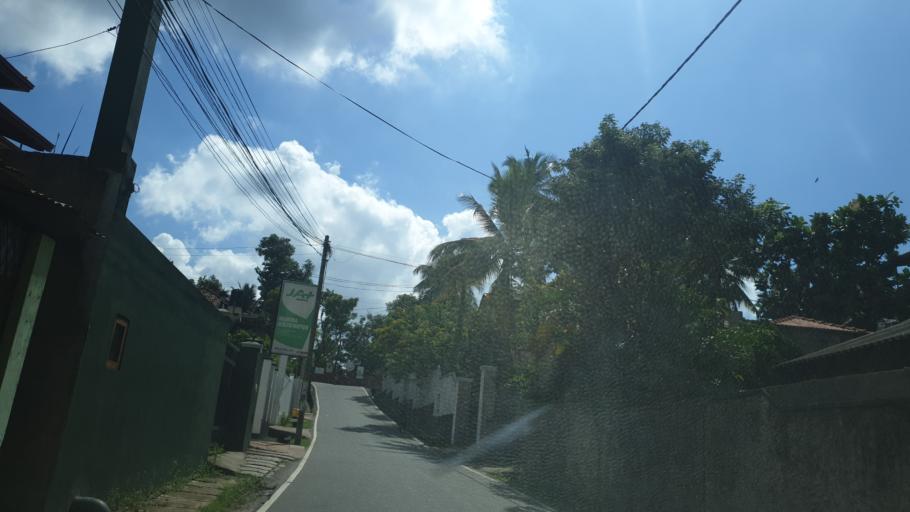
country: LK
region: Western
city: Moratuwa
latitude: 6.7930
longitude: 79.9103
